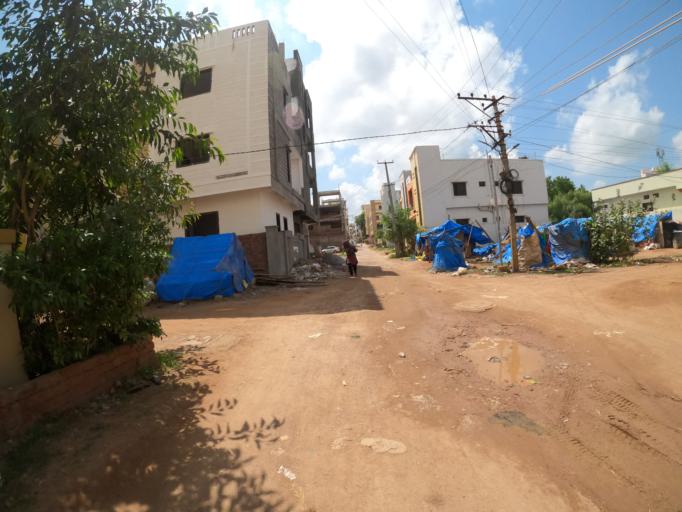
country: IN
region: Telangana
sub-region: Hyderabad
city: Hyderabad
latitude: 17.3627
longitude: 78.3856
